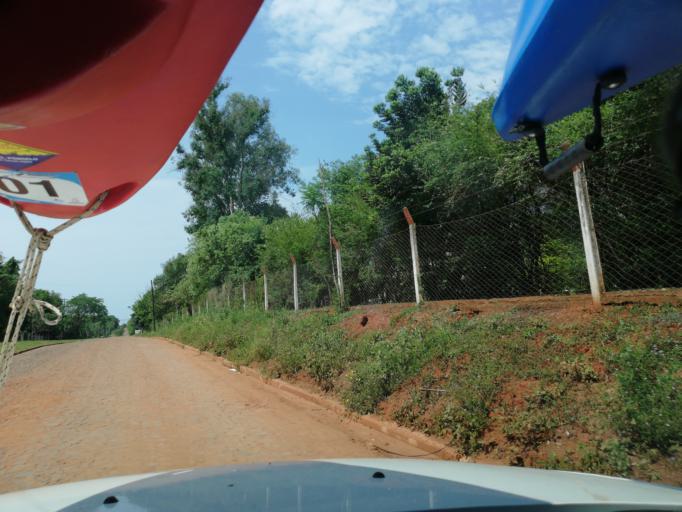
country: AR
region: Misiones
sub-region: Departamento de San Ignacio
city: San Ignacio
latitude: -27.2621
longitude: -55.5475
